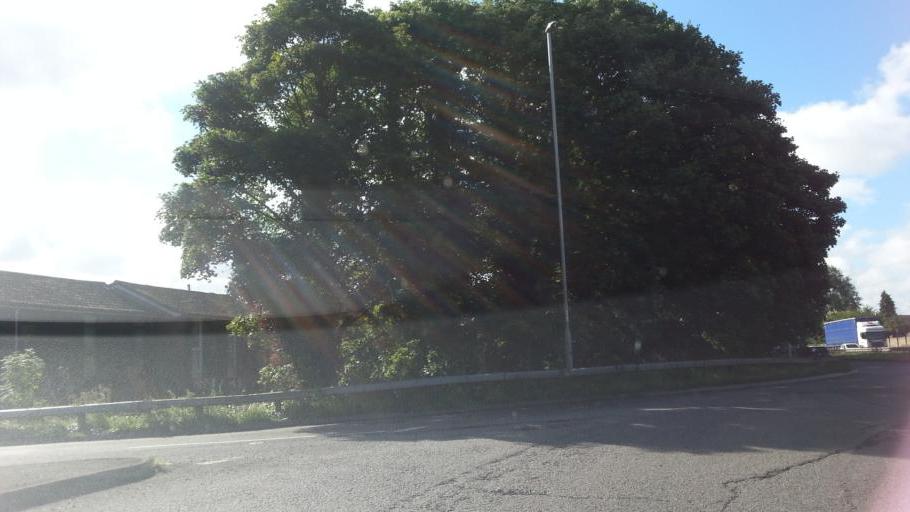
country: GB
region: England
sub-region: Northamptonshire
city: Northampton
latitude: 52.2648
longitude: -0.8427
